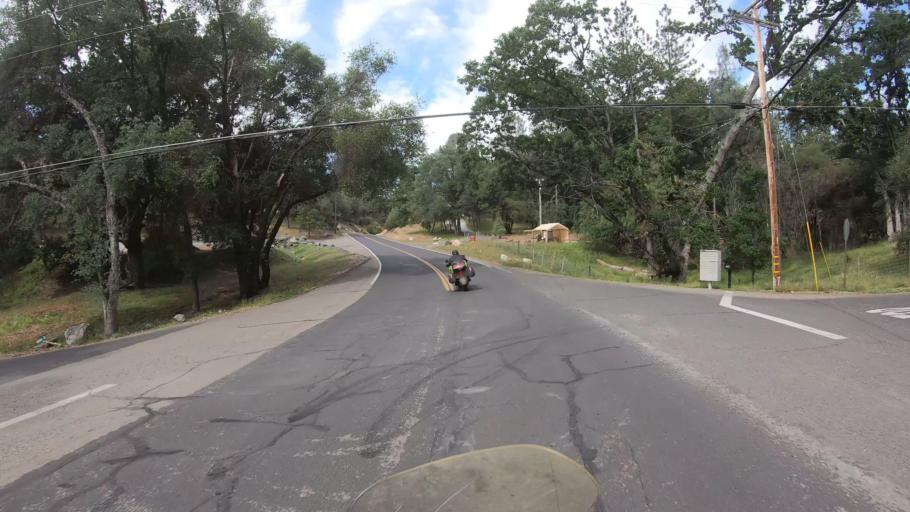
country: US
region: California
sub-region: Tuolumne County
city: Tuolumne City
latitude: 37.8604
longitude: -120.1939
